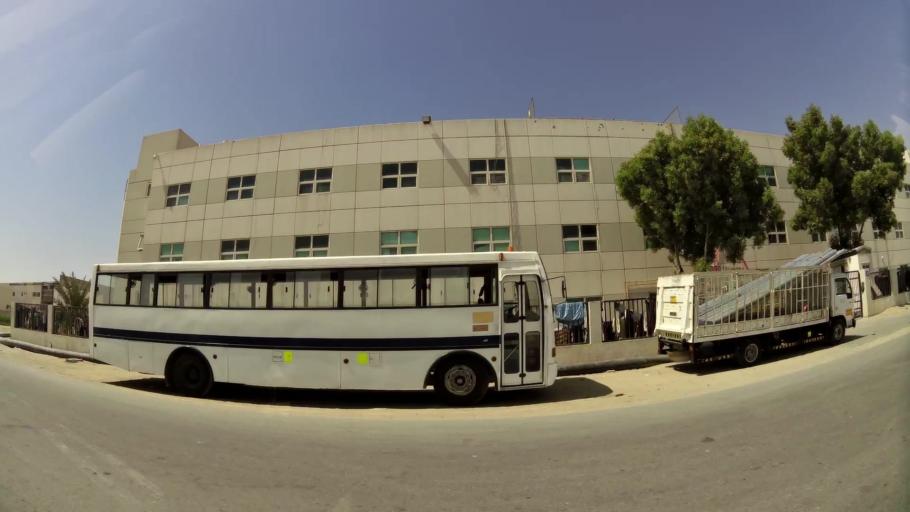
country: AE
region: Dubai
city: Dubai
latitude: 24.9776
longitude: 55.1556
